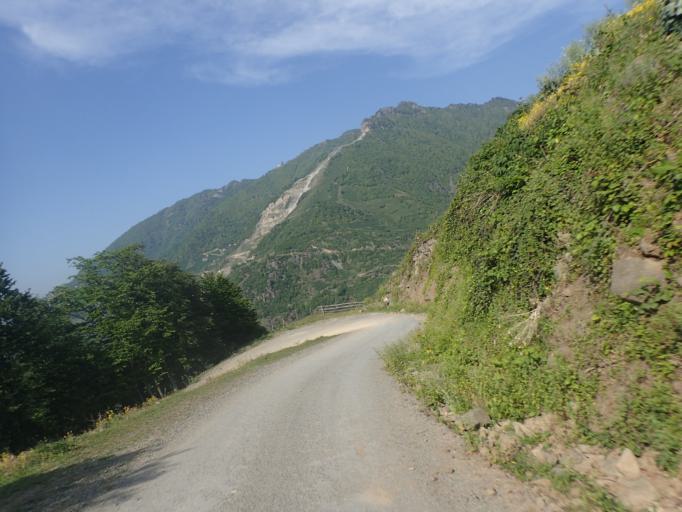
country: TR
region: Ordu
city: Topcam
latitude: 40.7101
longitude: 37.8589
